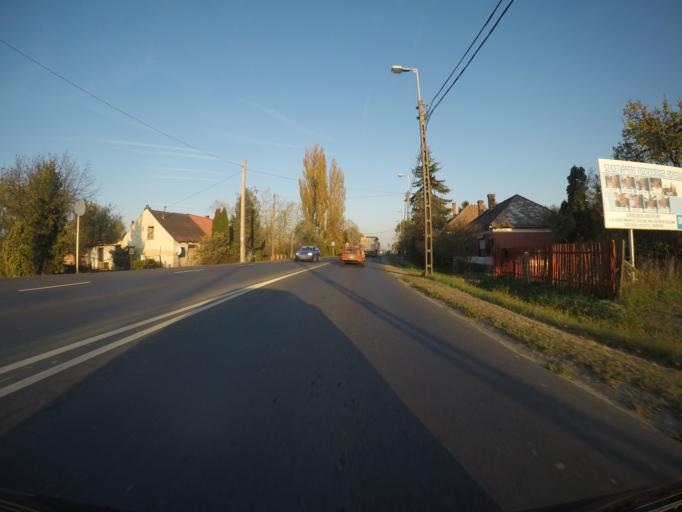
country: HU
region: Baranya
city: Szigetvar
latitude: 46.0486
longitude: 17.8211
